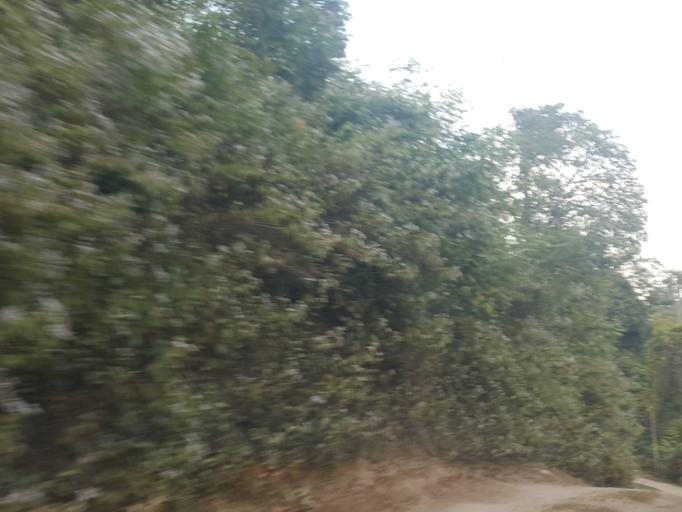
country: TH
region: Chiang Mai
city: Om Koi
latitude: 17.7769
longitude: 98.2990
